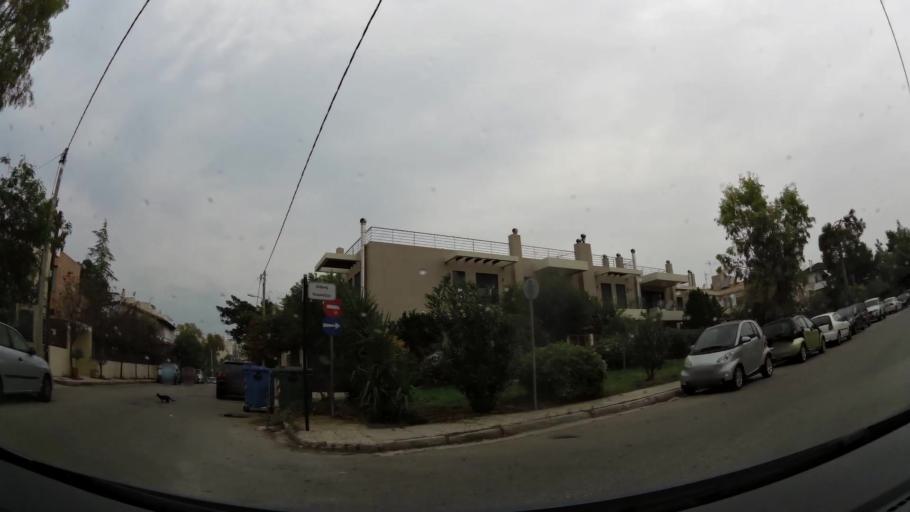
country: GR
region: Attica
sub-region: Nomarchia Athinas
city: Alimos
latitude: 37.9076
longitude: 23.7202
